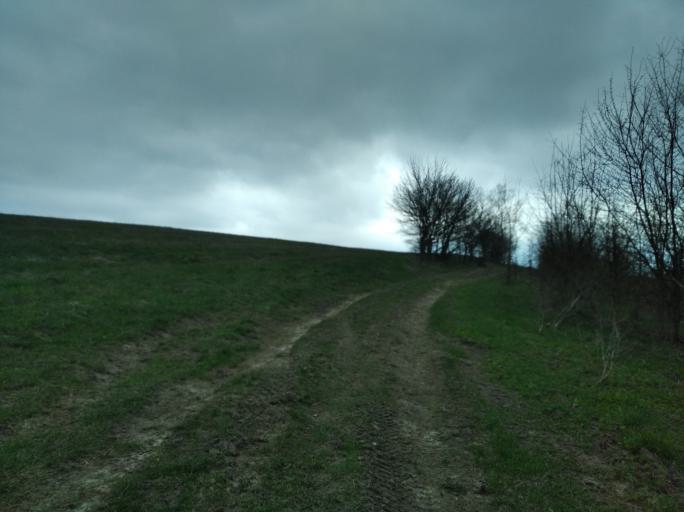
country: PL
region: Subcarpathian Voivodeship
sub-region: Powiat strzyzowski
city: Jawornik
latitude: 49.8146
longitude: 21.9015
